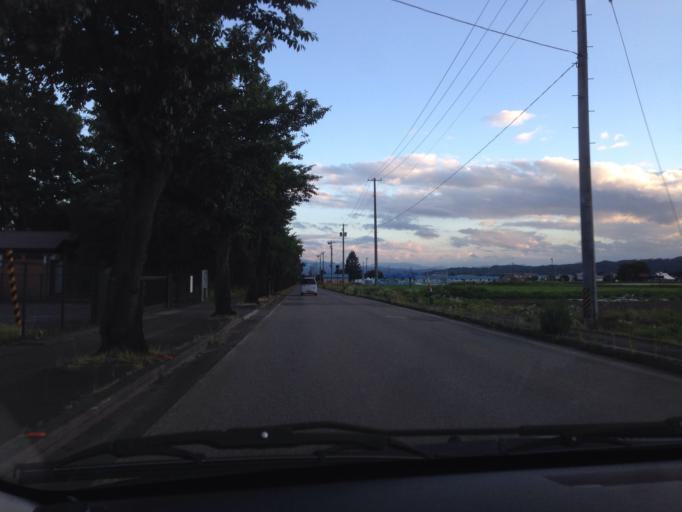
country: JP
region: Fukushima
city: Kitakata
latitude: 37.6564
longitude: 139.8636
